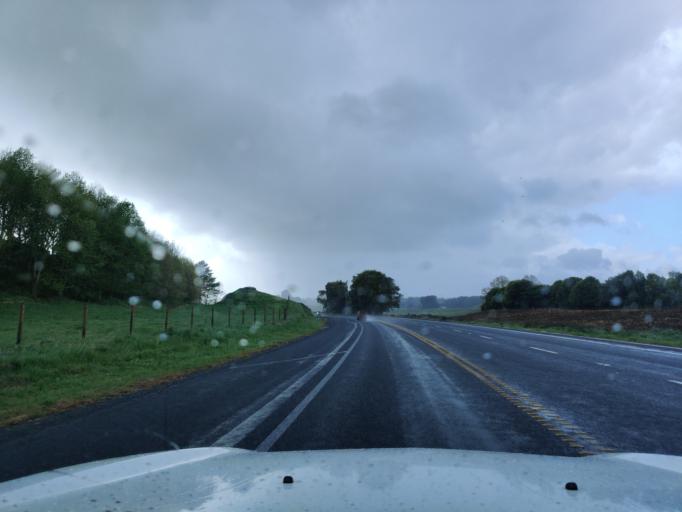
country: NZ
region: Waikato
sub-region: Waipa District
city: Cambridge
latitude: -37.9440
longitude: 175.5849
